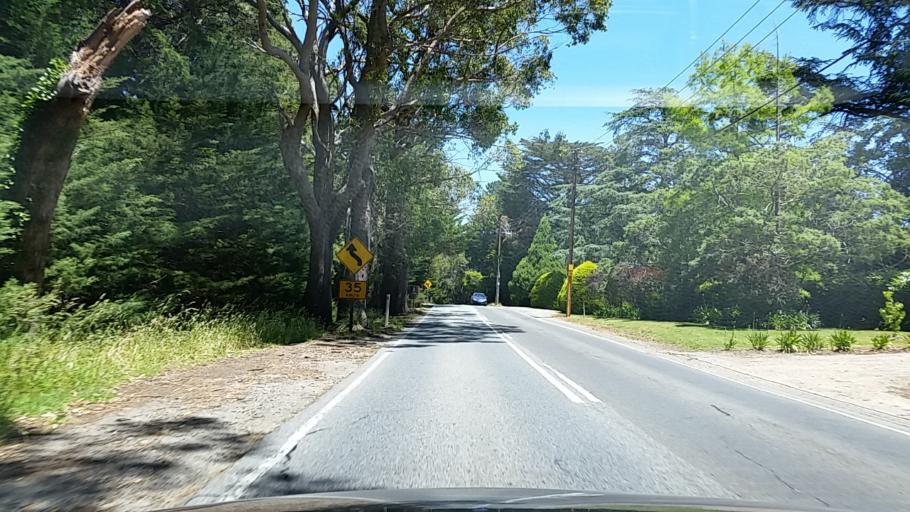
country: AU
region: South Australia
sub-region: Adelaide Hills
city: Crafers
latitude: -35.0051
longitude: 138.6996
